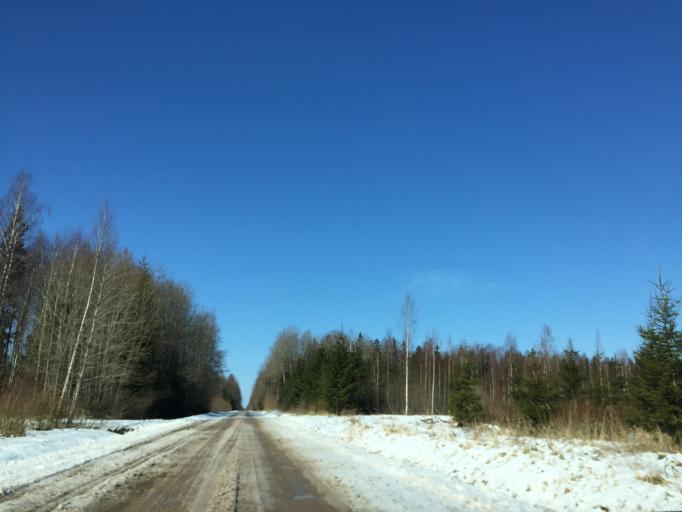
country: LV
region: Salacgrivas
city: Ainazi
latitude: 58.0277
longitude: 24.5587
